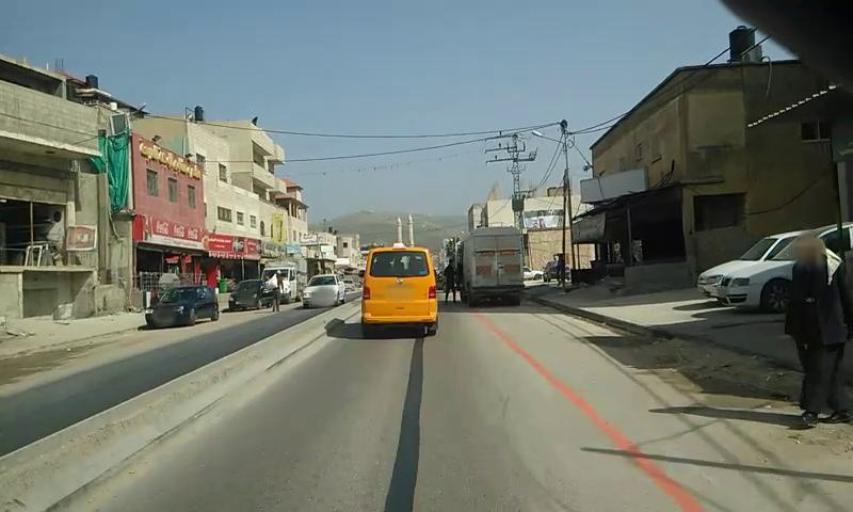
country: PS
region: West Bank
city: Huwwarah
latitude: 32.1526
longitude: 35.2589
